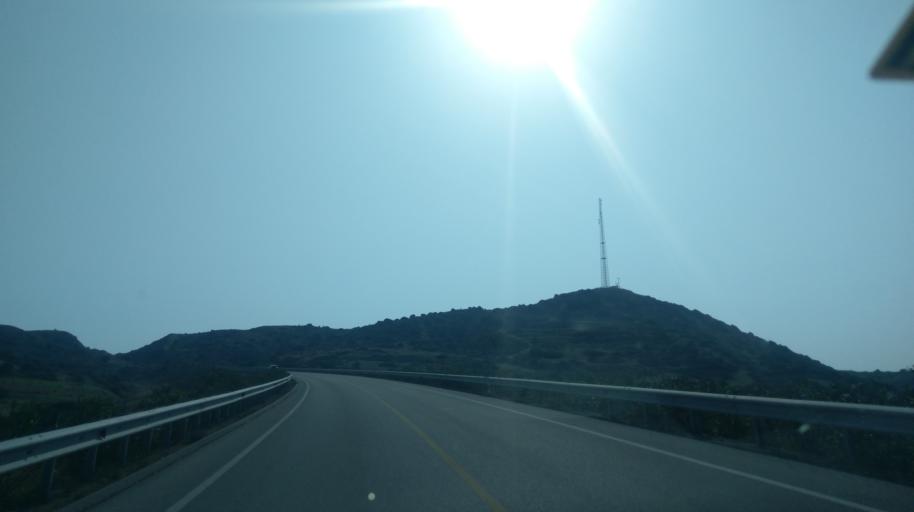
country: CY
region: Ammochostos
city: Leonarisso
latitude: 35.4920
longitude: 34.0978
